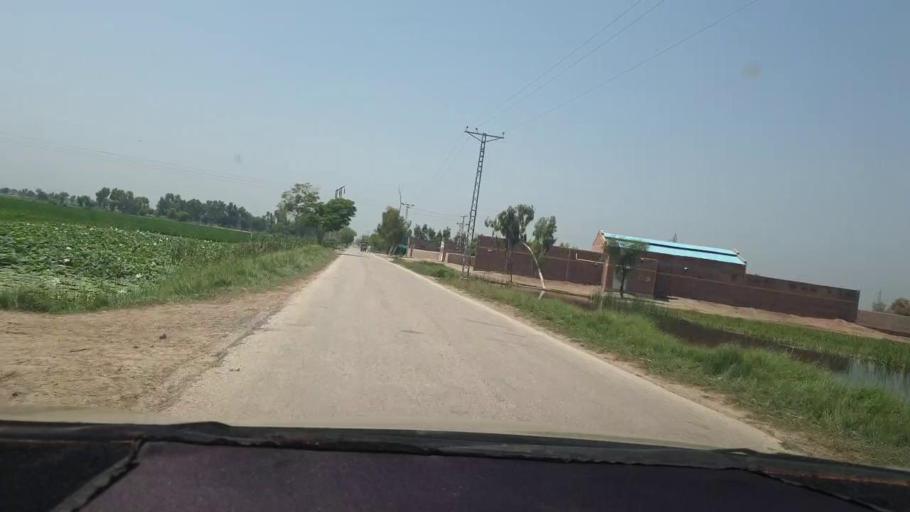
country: PK
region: Sindh
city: Kambar
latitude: 27.6006
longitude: 68.0285
